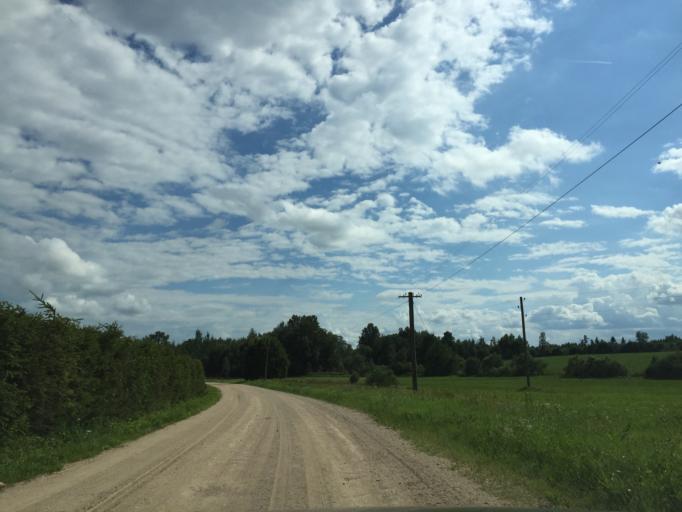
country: LV
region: Malpils
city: Malpils
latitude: 56.8473
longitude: 25.0497
